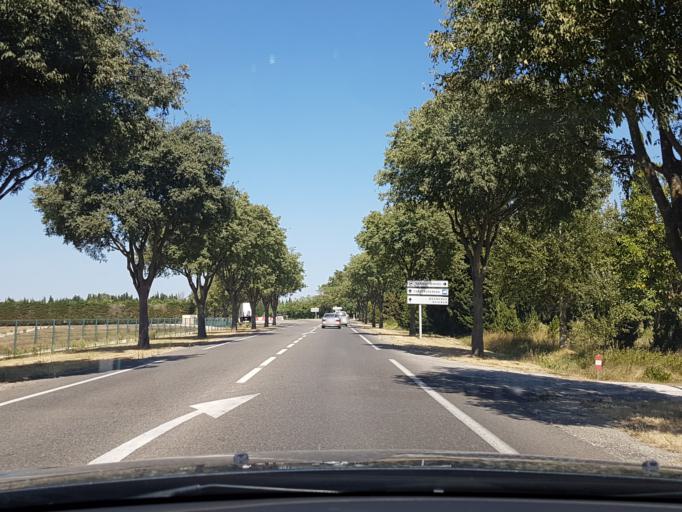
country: FR
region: Provence-Alpes-Cote d'Azur
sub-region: Departement des Bouches-du-Rhone
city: Eyragues
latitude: 43.8460
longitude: 4.8404
